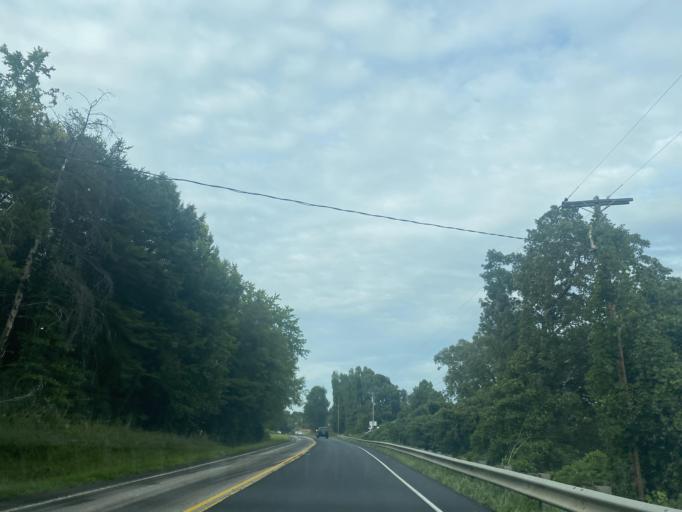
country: US
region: South Carolina
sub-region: Cherokee County
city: Blacksburg
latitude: 35.0961
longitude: -81.5512
